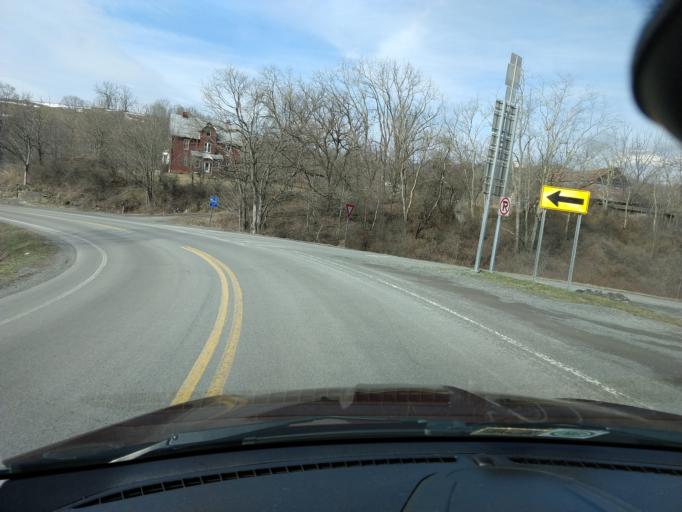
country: US
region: West Virginia
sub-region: Pocahontas County
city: Marlinton
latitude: 38.1582
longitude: -80.1808
